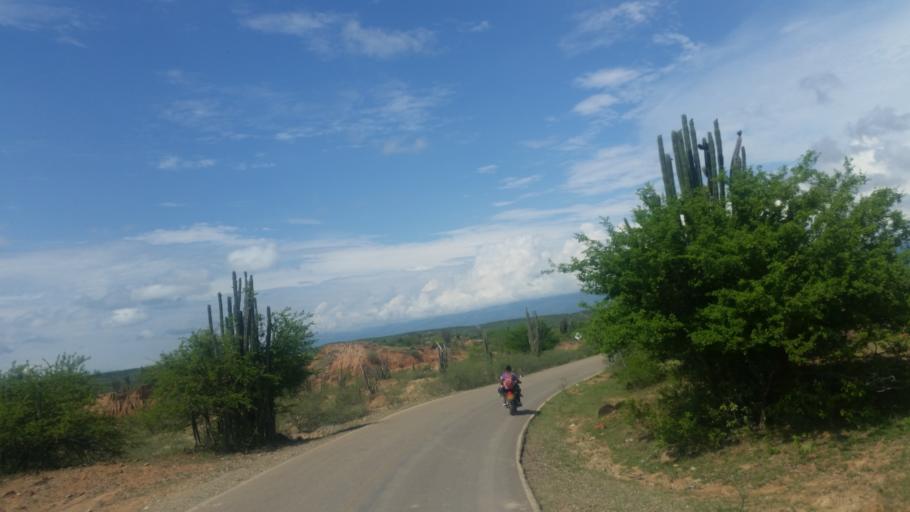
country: CO
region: Huila
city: Villavieja
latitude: 3.2314
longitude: -75.1776
